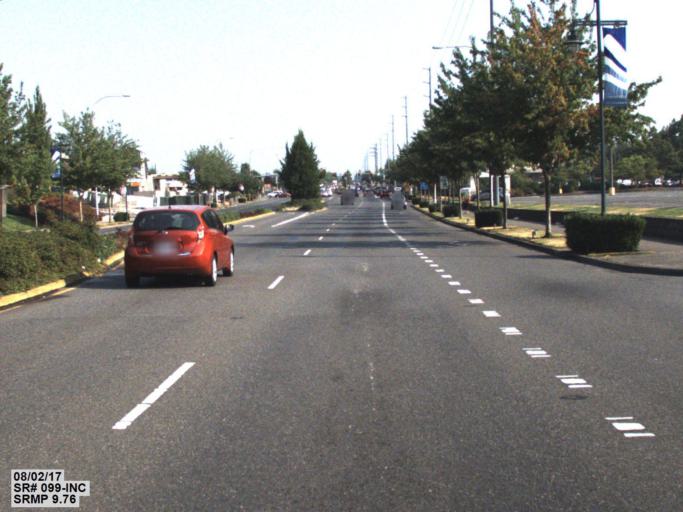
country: US
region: Washington
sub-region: King County
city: Federal Way
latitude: 47.3127
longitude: -122.3133
